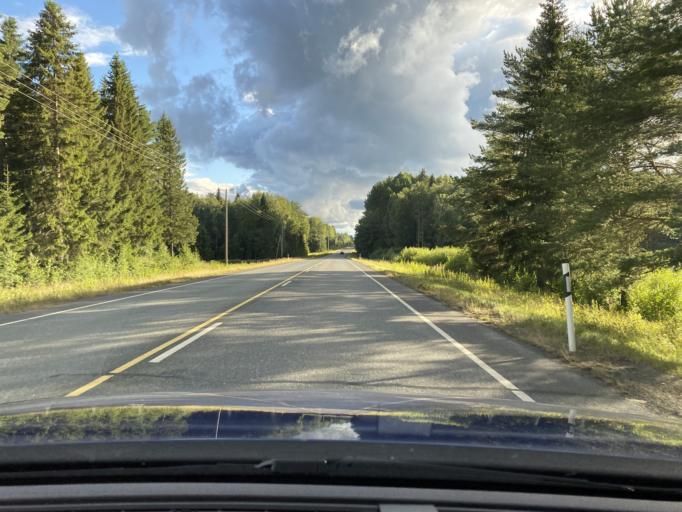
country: FI
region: Haeme
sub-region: Haemeenlinna
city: Renko
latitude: 60.8733
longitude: 24.2163
